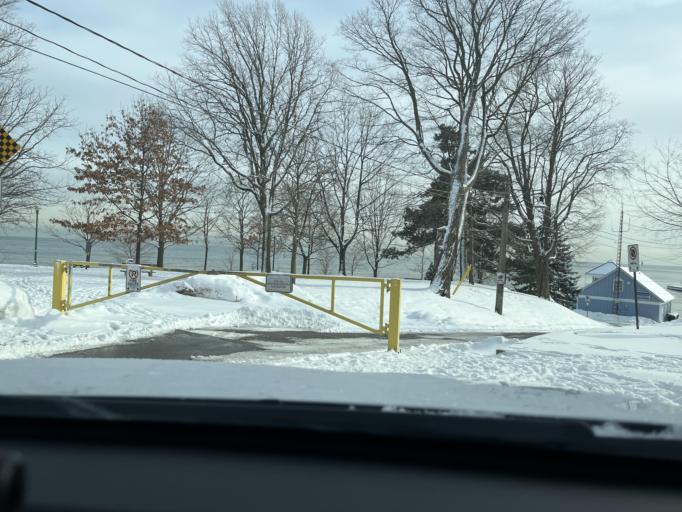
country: CA
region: Ontario
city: Oakville
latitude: 43.4420
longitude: -79.6665
